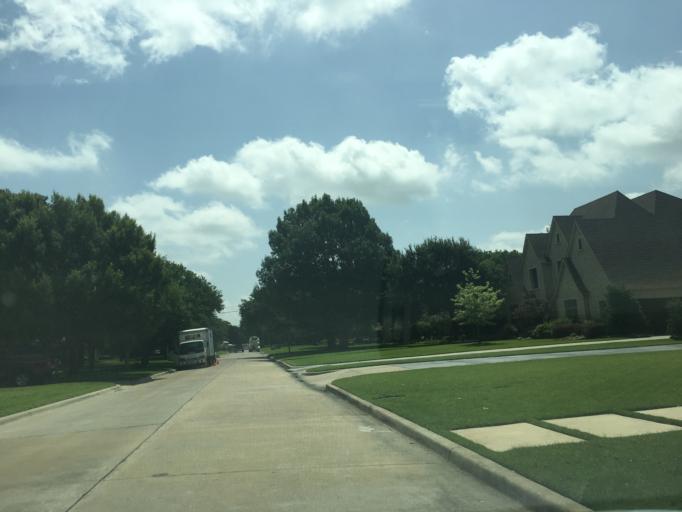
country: US
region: Texas
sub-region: Dallas County
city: University Park
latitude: 32.8770
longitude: -96.8009
